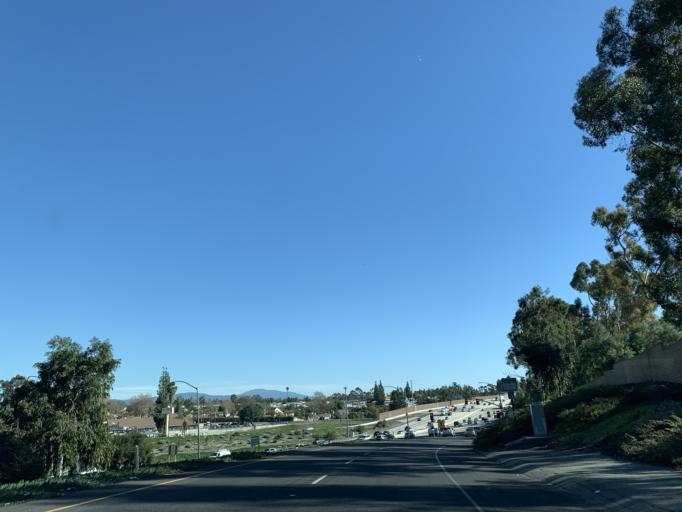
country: US
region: California
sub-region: Orange County
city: Brea
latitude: 33.9102
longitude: -117.8844
